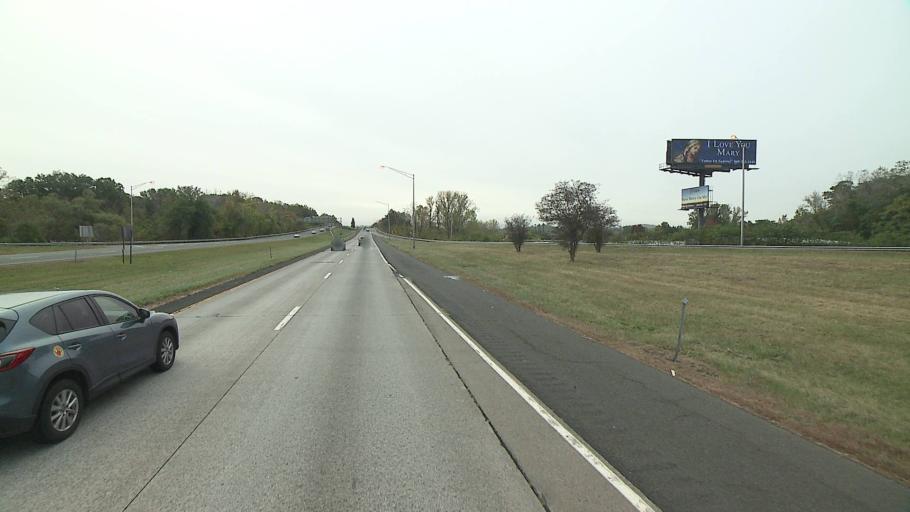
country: US
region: Connecticut
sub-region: Hartford County
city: New Britain
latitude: 41.6553
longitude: -72.7717
